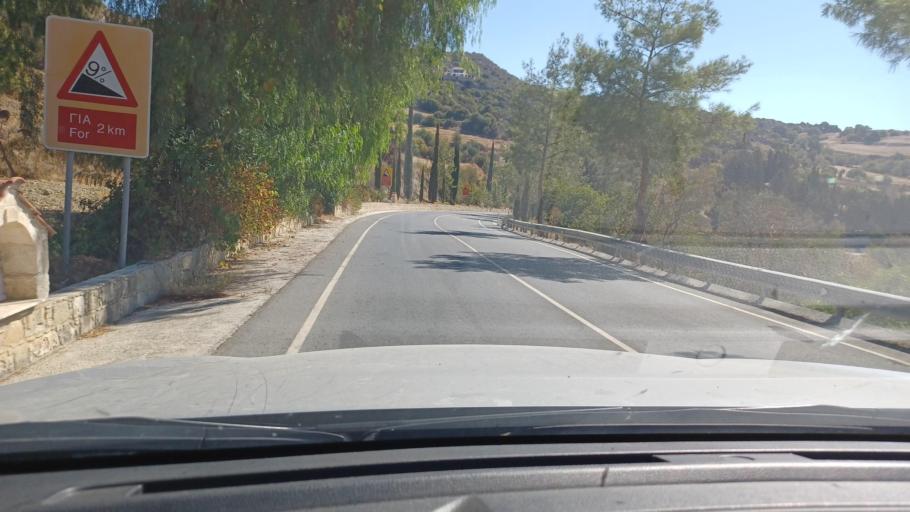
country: CY
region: Pafos
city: Polis
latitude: 34.9878
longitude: 32.4869
